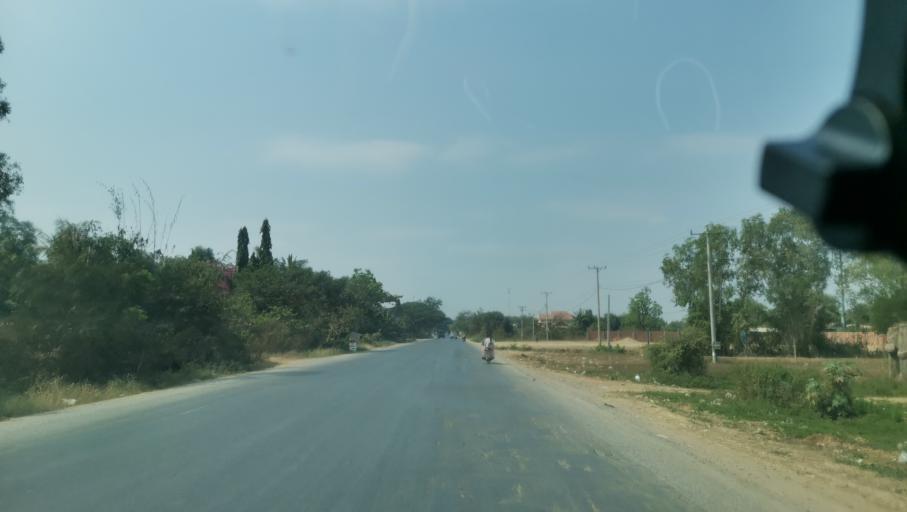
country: KH
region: Battambang
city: Battambang
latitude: 13.0708
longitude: 103.1665
